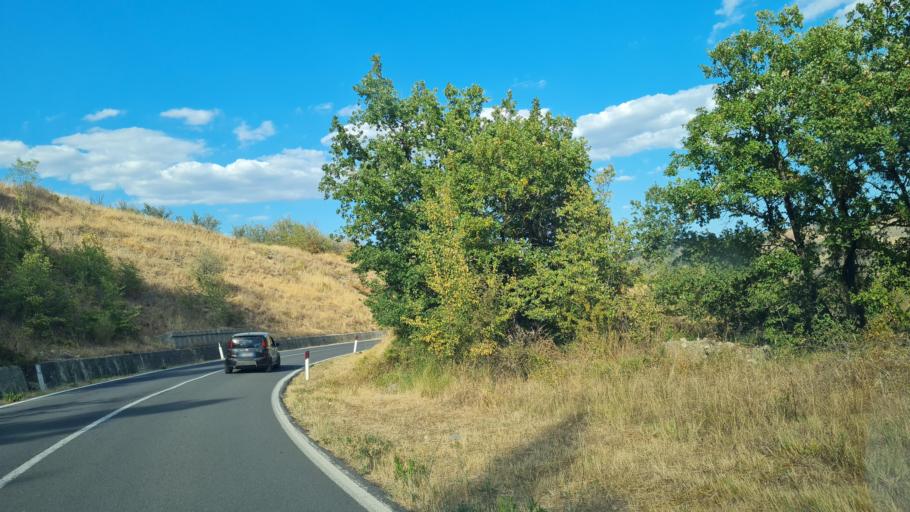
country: IT
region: Tuscany
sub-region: Provincia di Siena
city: Abbadia San Salvatore
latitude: 42.9353
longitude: 11.7017
